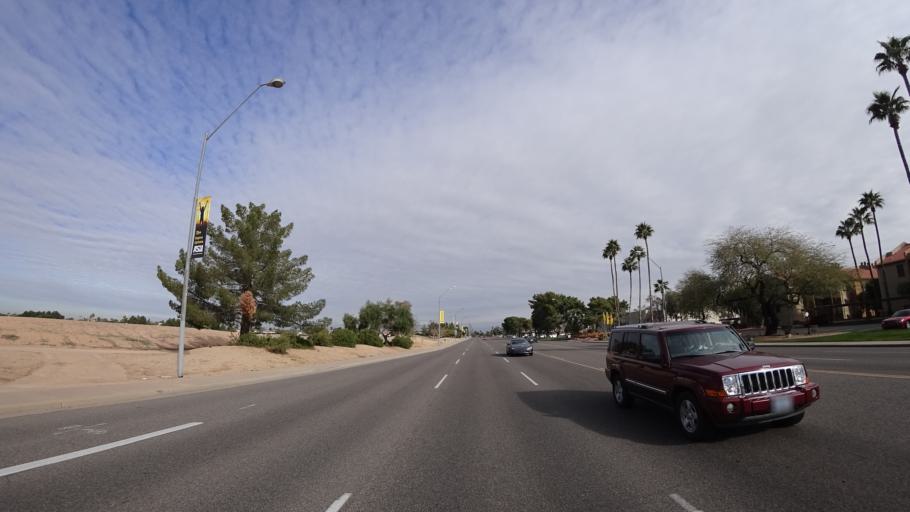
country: US
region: Arizona
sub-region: Maricopa County
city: Glendale
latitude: 33.6077
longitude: -112.1514
